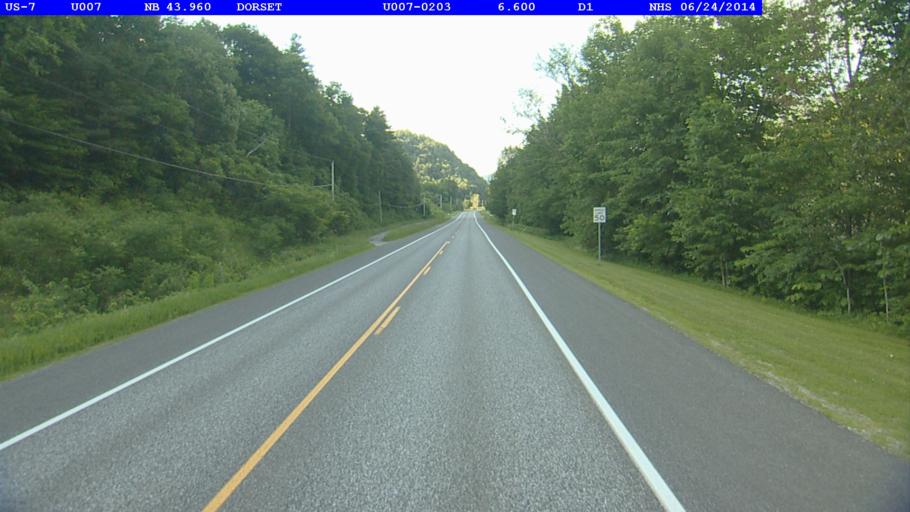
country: US
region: Vermont
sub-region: Bennington County
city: Manchester Center
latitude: 43.3035
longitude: -72.9952
